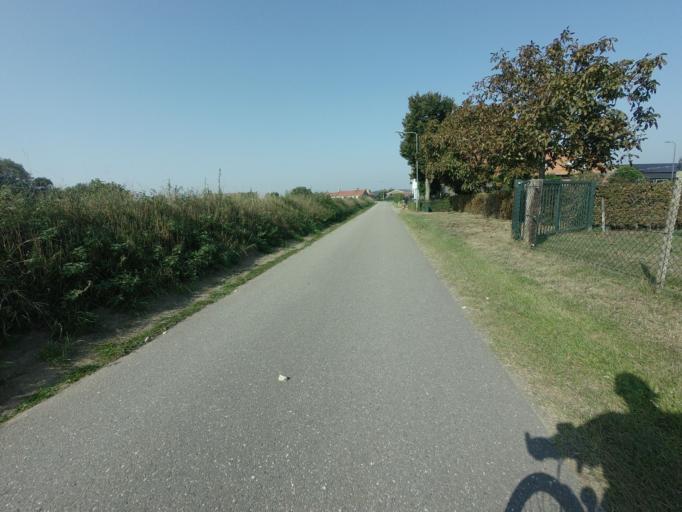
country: NL
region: Limburg
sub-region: Gemeente Beesel
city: Beesel
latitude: 51.2581
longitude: 6.0163
